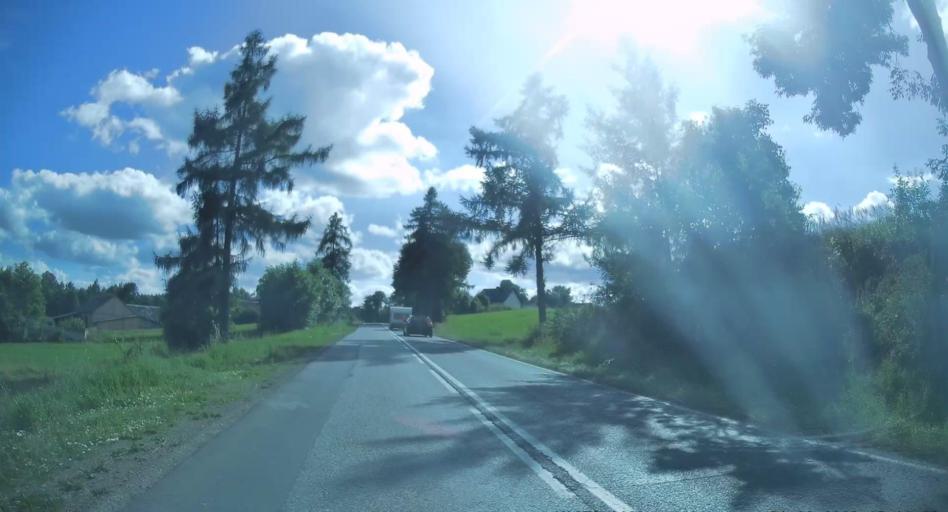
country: PL
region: Swietokrzyskie
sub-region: Powiat kielecki
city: Nowa Slupia
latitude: 50.8289
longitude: 21.0797
